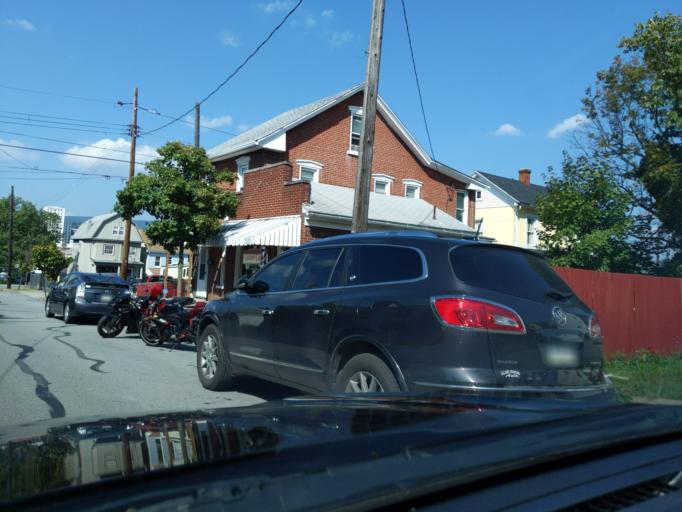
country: US
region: Pennsylvania
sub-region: Blair County
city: Altoona
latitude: 40.5160
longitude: -78.3905
